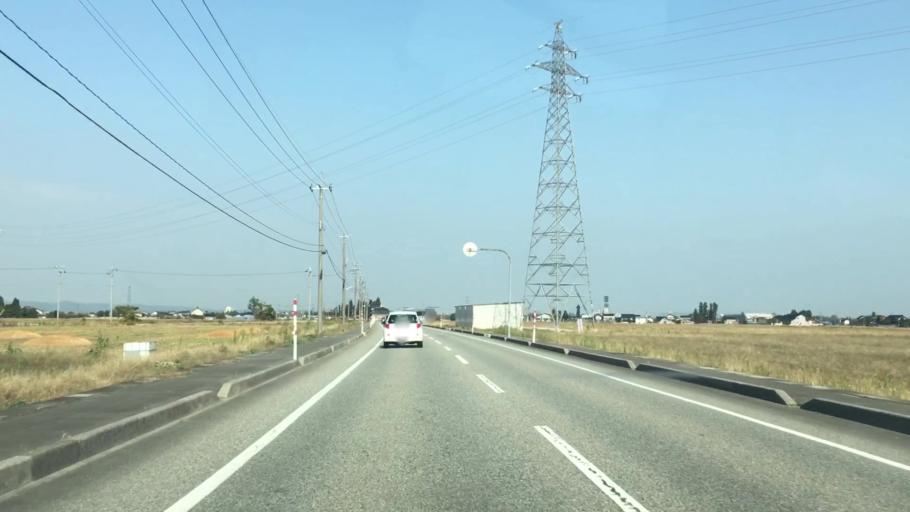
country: JP
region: Toyama
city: Yatsuomachi-higashikumisaka
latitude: 36.6056
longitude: 137.1921
